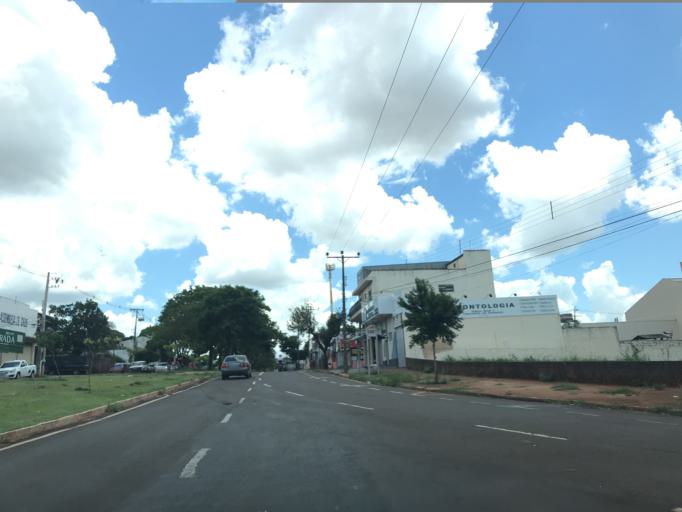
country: BR
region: Parana
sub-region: Maringa
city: Maringa
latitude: -23.3904
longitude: -51.9161
